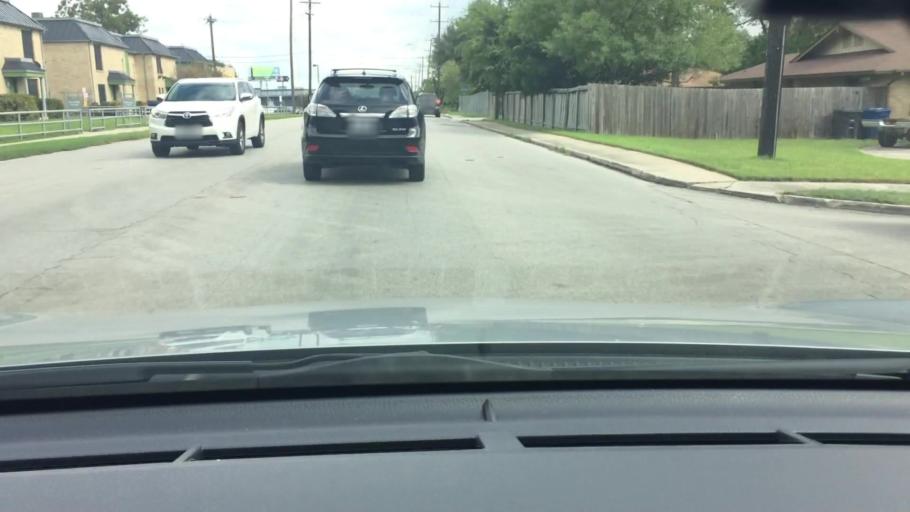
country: US
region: Texas
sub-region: Bexar County
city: Castle Hills
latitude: 29.5438
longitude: -98.5315
